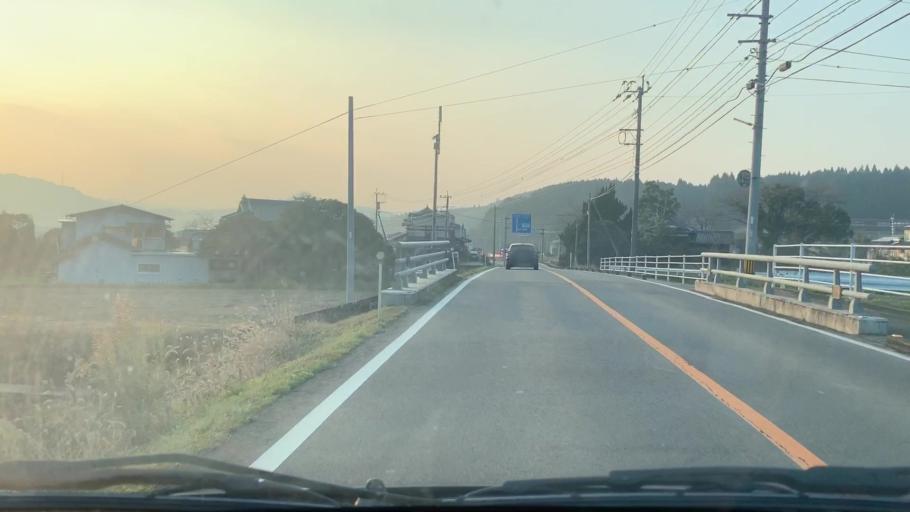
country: JP
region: Saga Prefecture
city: Takeocho-takeo
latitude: 33.2556
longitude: 130.0053
